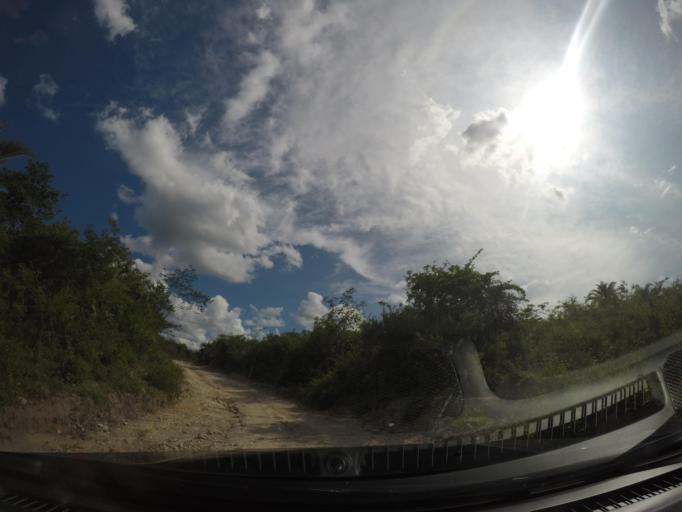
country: BR
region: Bahia
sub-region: Barra Da Estiva
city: Barra da Estiva
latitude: -13.1407
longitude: -41.5964
